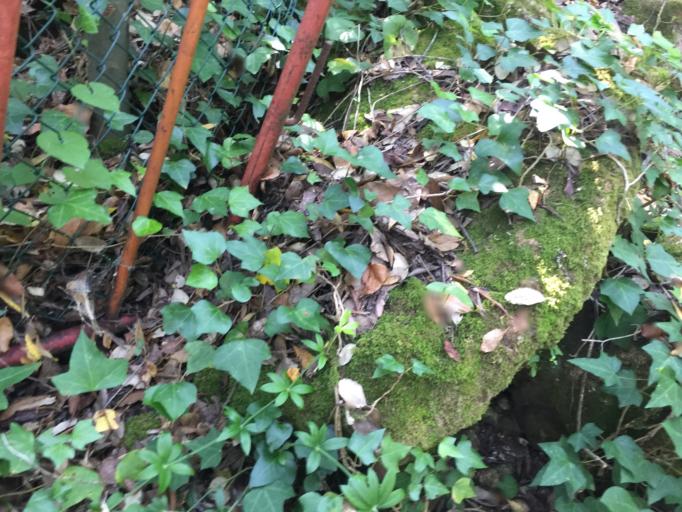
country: PT
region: Lisbon
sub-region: Mafra
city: Milharado
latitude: 38.9054
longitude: -9.1870
